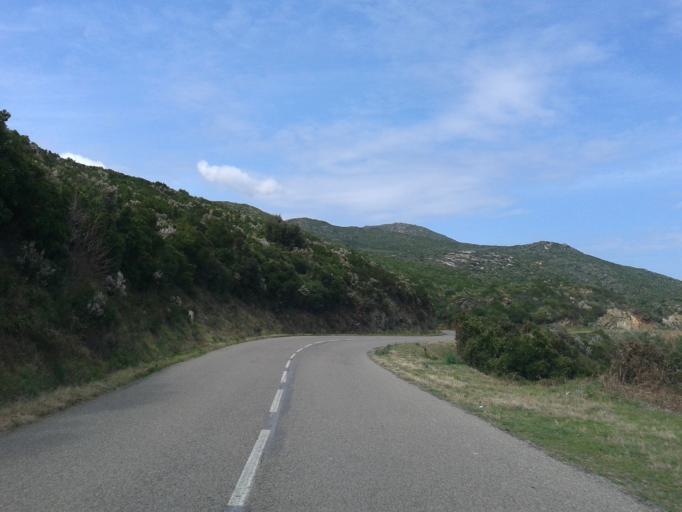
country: FR
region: Corsica
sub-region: Departement de la Haute-Corse
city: Brando
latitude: 42.8426
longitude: 9.4833
